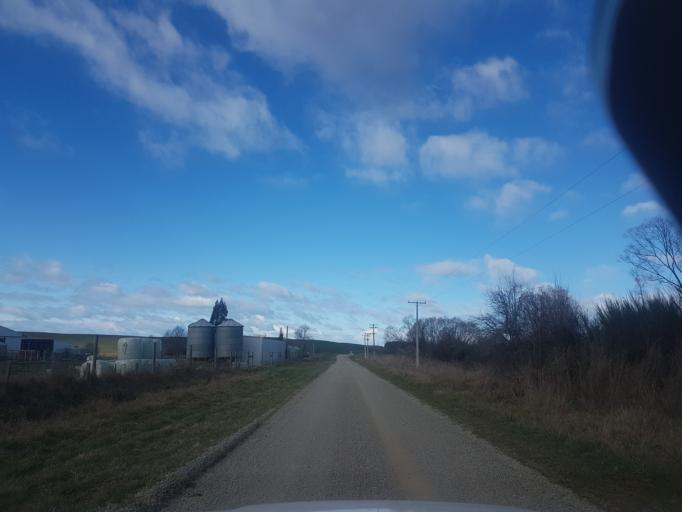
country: NZ
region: Canterbury
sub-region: Timaru District
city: Pleasant Point
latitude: -44.1915
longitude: 171.2000
